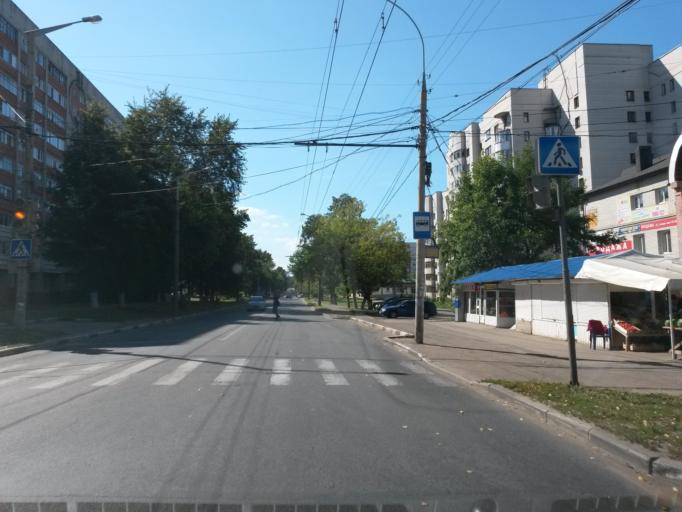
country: RU
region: Jaroslavl
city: Yaroslavl
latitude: 57.5856
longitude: 39.8417
